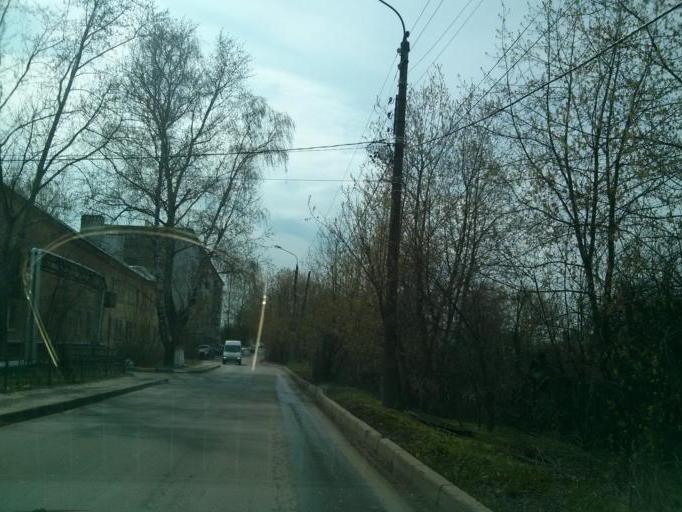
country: RU
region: Nizjnij Novgorod
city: Nizhniy Novgorod
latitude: 56.3112
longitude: 44.0509
